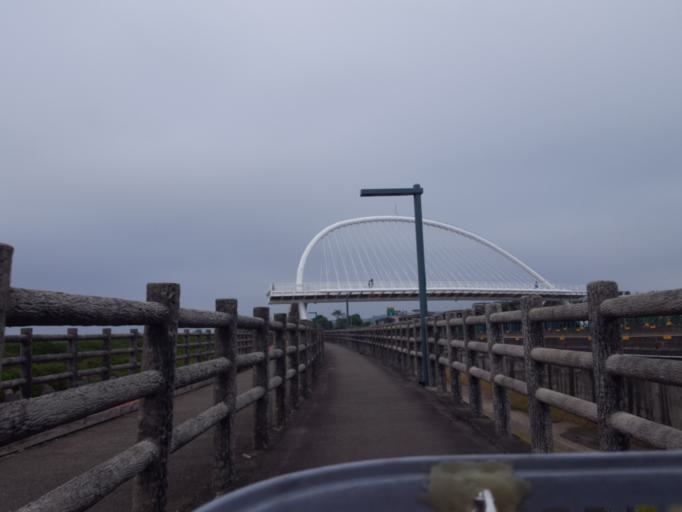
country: TW
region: Taiwan
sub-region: Hsinchu
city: Hsinchu
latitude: 24.7480
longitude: 120.9033
